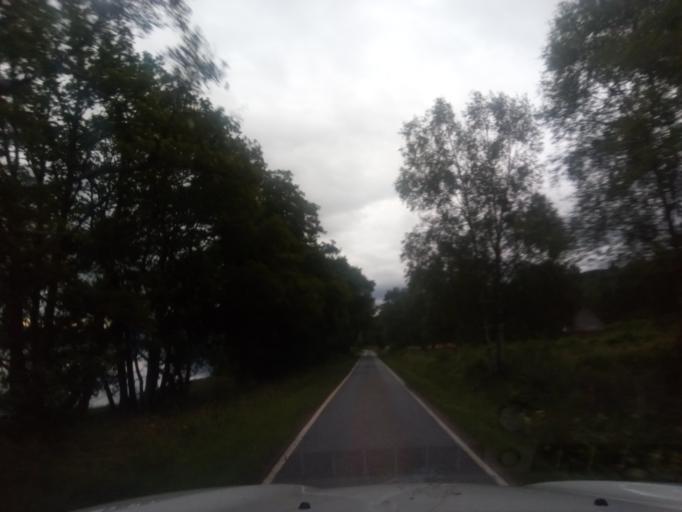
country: GB
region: Scotland
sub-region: Highland
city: Fort William
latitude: 56.8465
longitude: -5.2851
